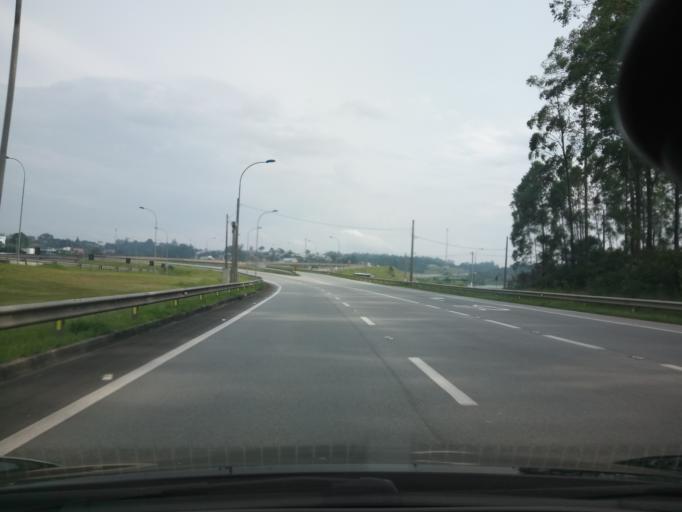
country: BR
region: Sao Paulo
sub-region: Sao Bernardo Do Campo
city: Sao Bernardo do Campo
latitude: -23.7613
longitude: -46.5936
